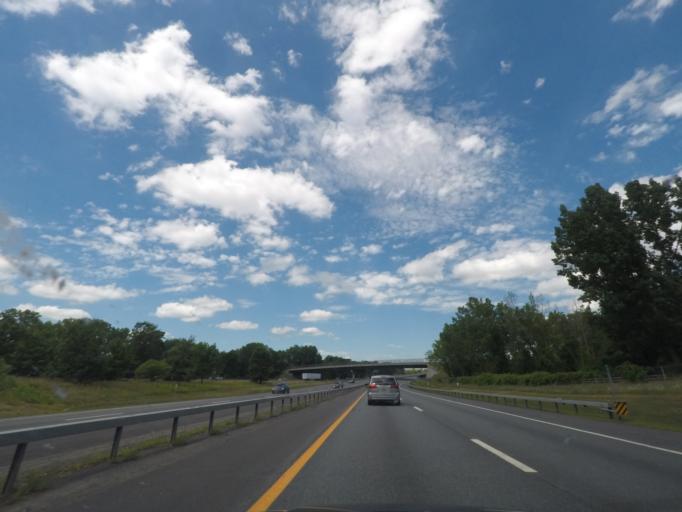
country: US
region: New York
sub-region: Albany County
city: McKownville
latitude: 42.7023
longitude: -73.8477
